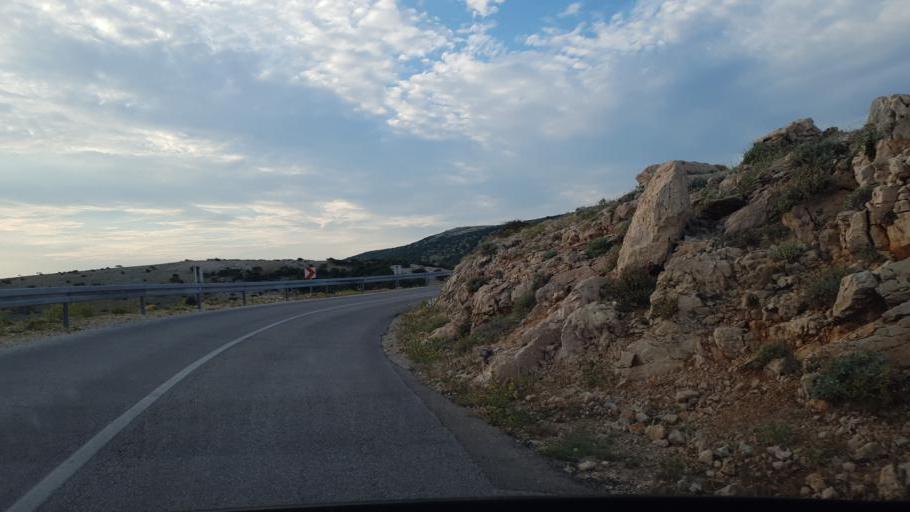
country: HR
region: Primorsko-Goranska
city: Punat
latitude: 44.9757
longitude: 14.6566
